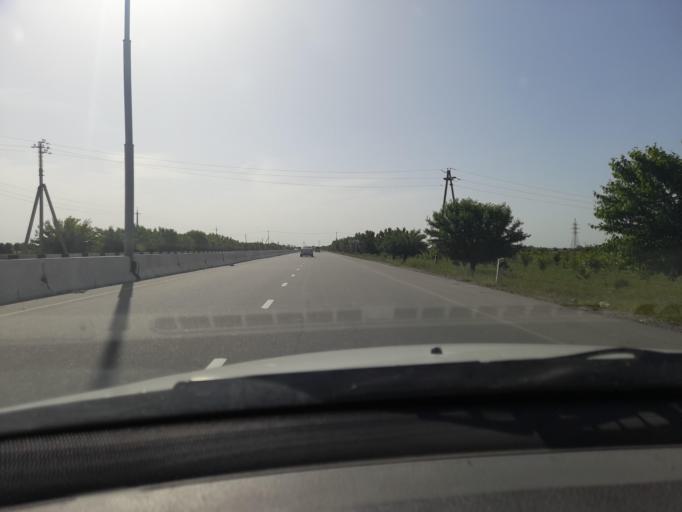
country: UZ
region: Samarqand
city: Ishtixon
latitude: 39.9569
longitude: 66.4732
